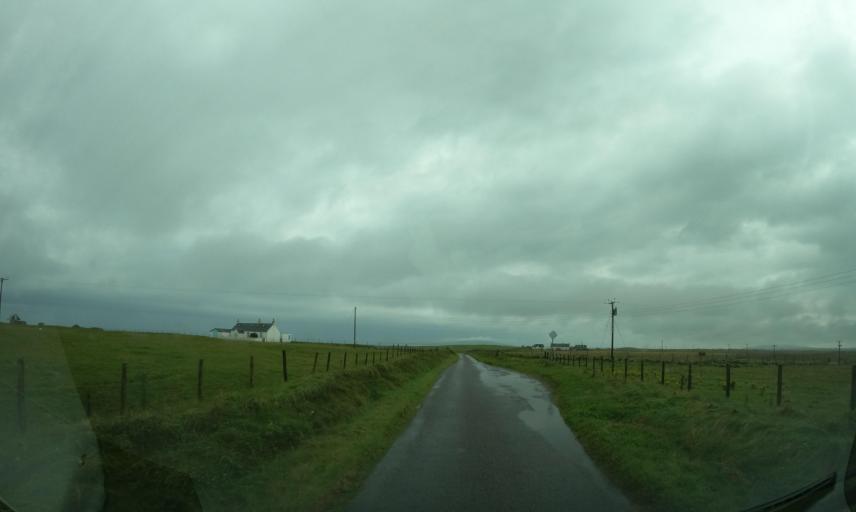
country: GB
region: Scotland
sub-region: Eilean Siar
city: Barra
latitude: 56.4940
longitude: -6.8184
